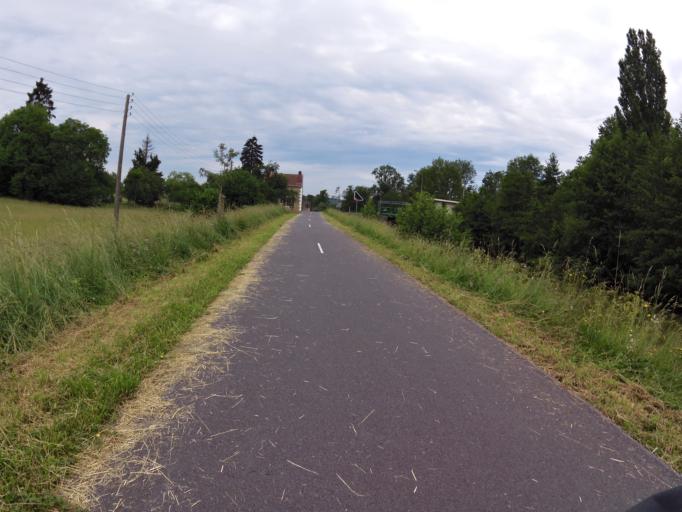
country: FR
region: Champagne-Ardenne
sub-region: Departement des Ardennes
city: Donchery
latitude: 49.6927
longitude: 4.8704
